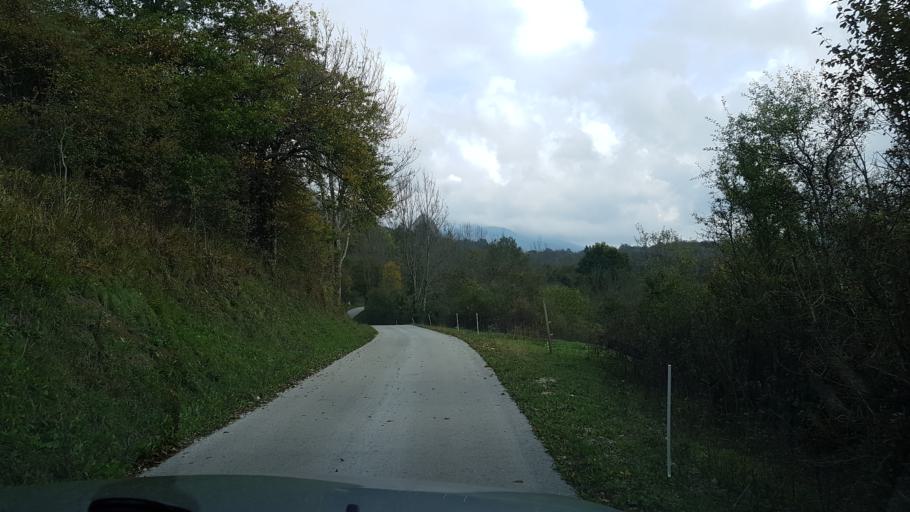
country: HR
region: Istarska
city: Buzet
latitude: 45.4229
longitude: 14.0778
